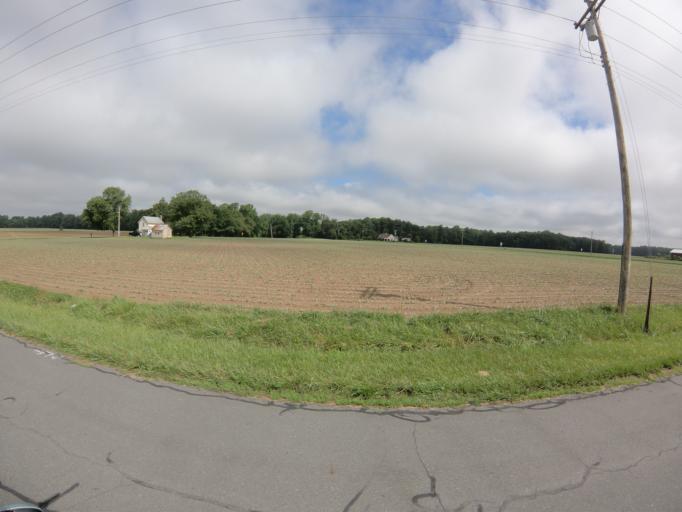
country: US
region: Delaware
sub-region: Kent County
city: Riverview
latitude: 39.0065
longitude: -75.5269
